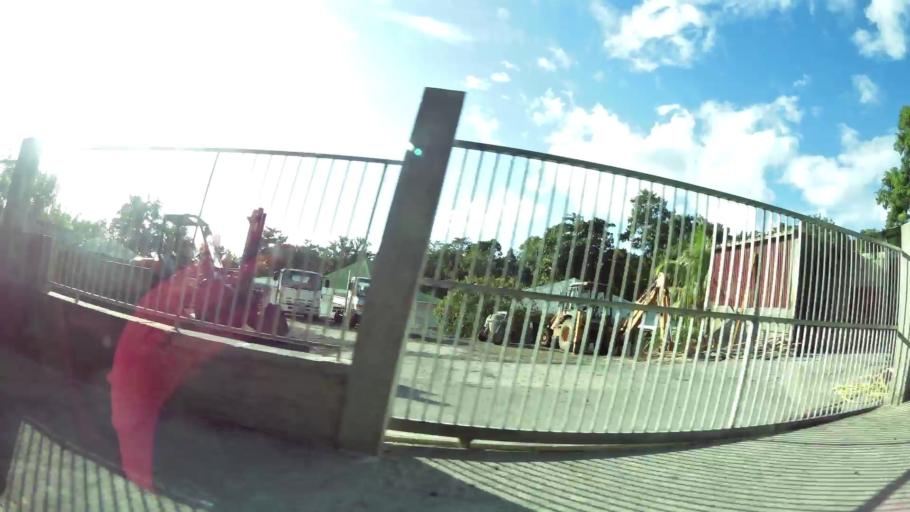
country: GP
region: Guadeloupe
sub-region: Guadeloupe
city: Pointe-Noire
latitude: 16.2474
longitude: -61.7908
